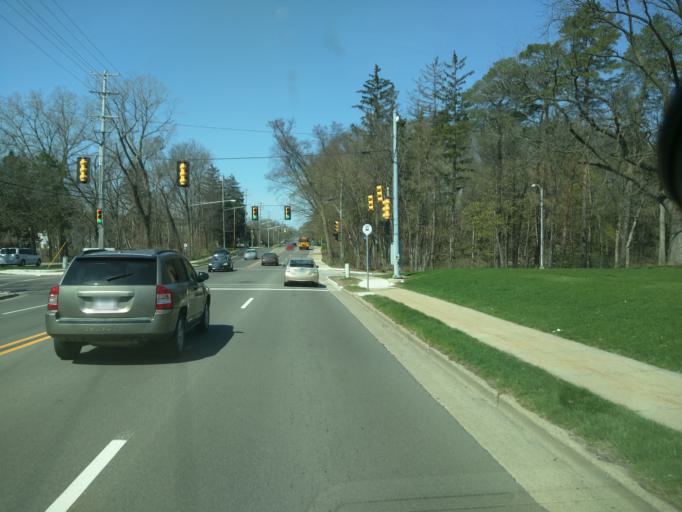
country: US
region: Michigan
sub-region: Kent County
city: East Grand Rapids
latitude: 42.9270
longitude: -85.5865
